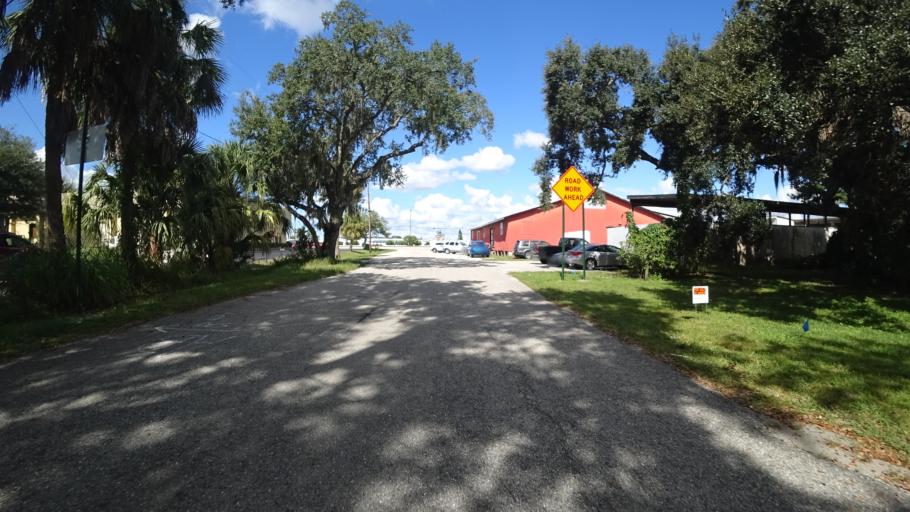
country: US
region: Florida
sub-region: Manatee County
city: Ellenton
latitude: 27.5210
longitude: -82.5197
